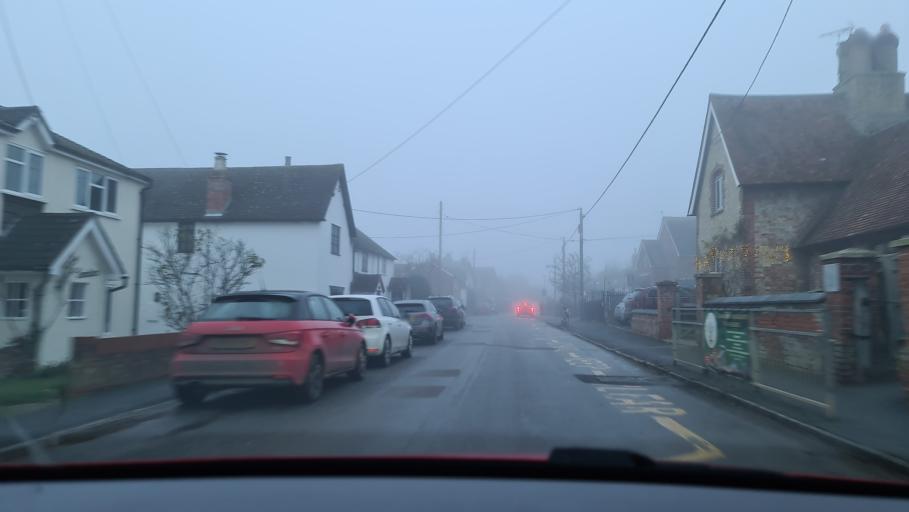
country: GB
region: England
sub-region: Buckinghamshire
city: Waddesdon
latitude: 51.8738
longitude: -0.9186
